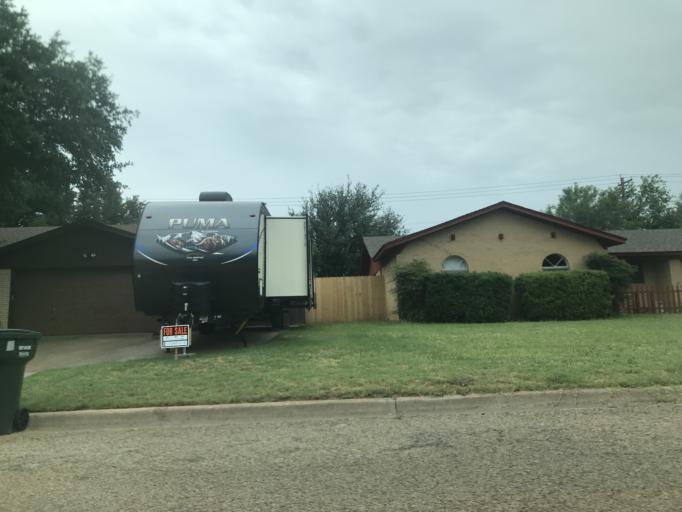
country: US
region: Texas
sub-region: Taylor County
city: Abilene
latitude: 32.4126
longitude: -99.7849
